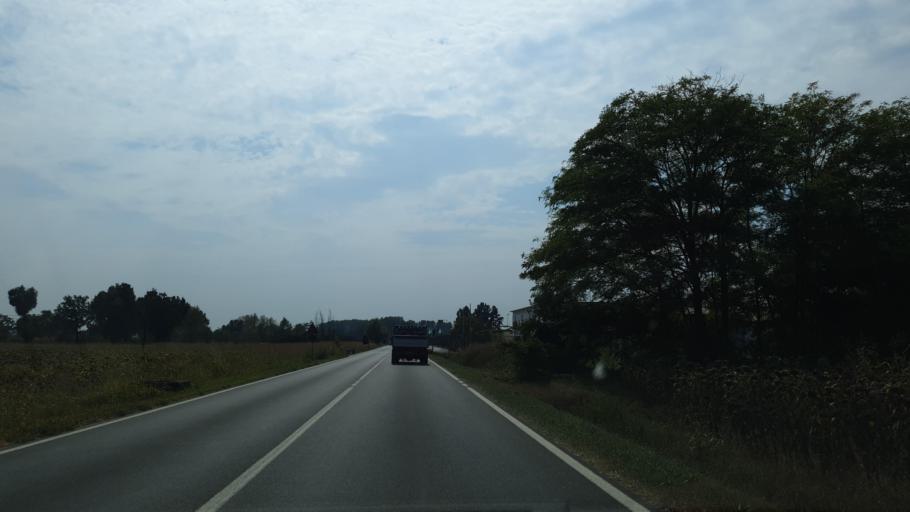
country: IT
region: Lombardy
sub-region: Provincia di Cremona
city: San Daniele Po
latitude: 45.0898
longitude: 10.1801
